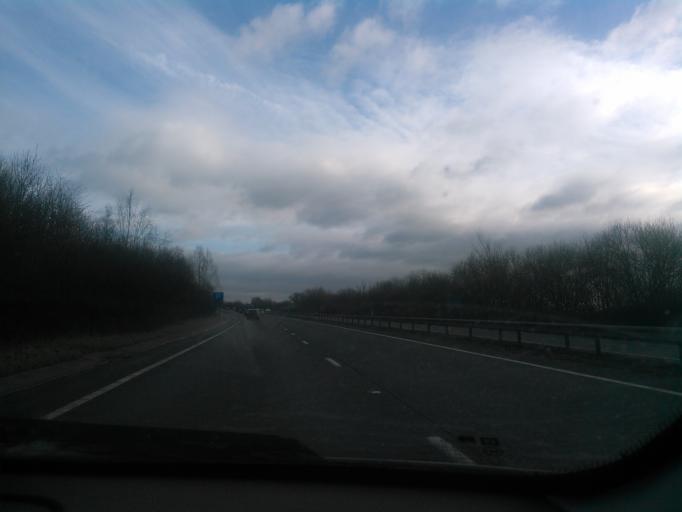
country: GB
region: England
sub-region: Derbyshire
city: Etwall
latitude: 52.8805
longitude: -1.6699
